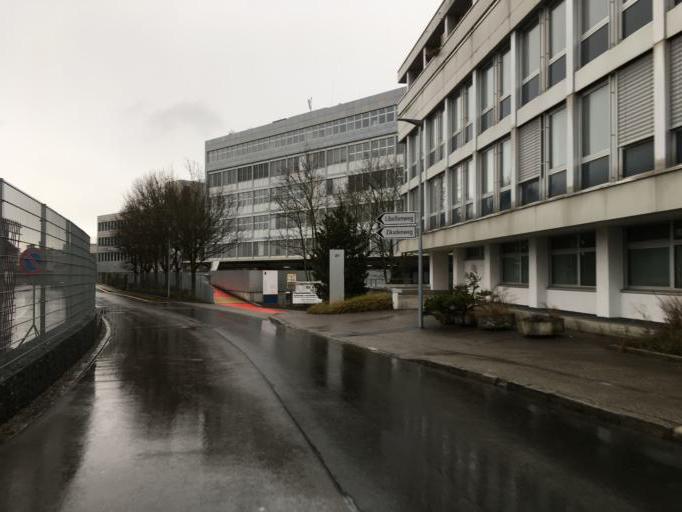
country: CH
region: Bern
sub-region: Bern-Mittelland District
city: Muri
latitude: 46.9551
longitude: 7.4741
